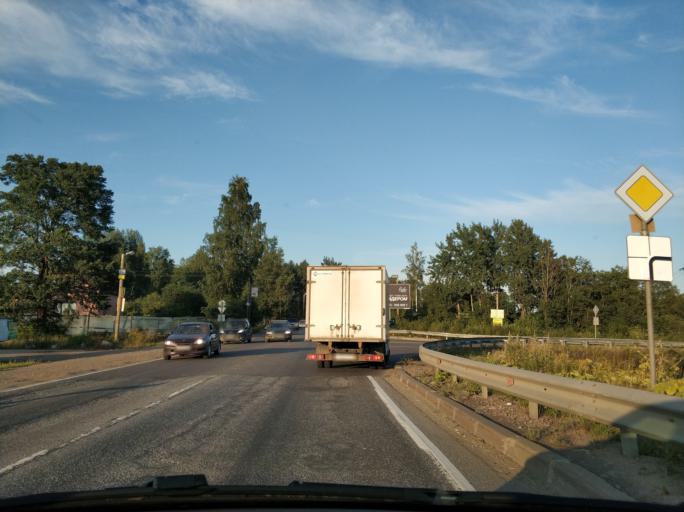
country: RU
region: Leningrad
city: Bugry
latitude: 60.1012
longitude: 30.3866
